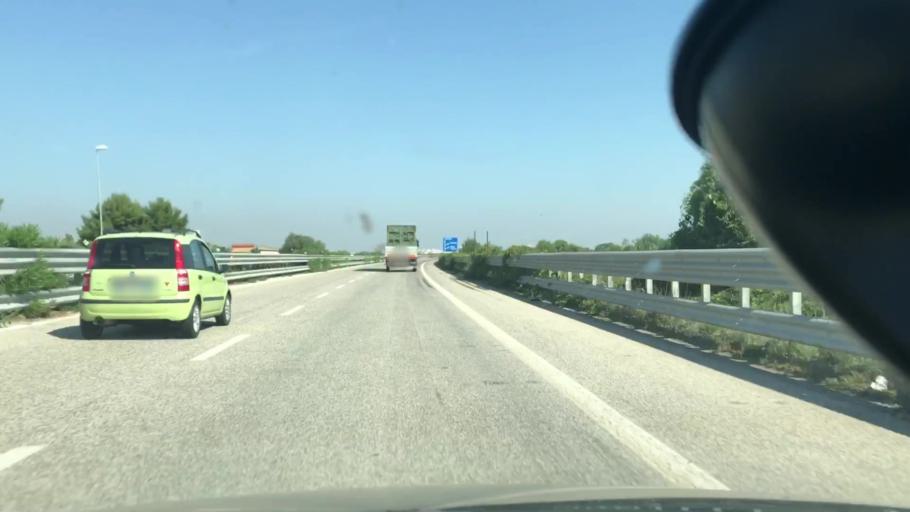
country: IT
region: Apulia
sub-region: Provincia di Foggia
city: Foggia
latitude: 41.4156
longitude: 15.5585
